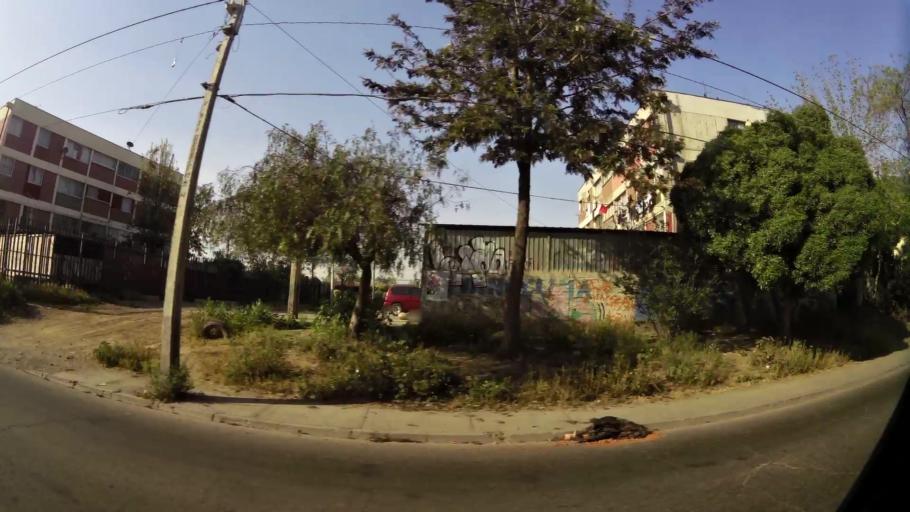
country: CL
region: Santiago Metropolitan
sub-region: Provincia de Santiago
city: Lo Prado
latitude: -33.4135
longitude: -70.7512
